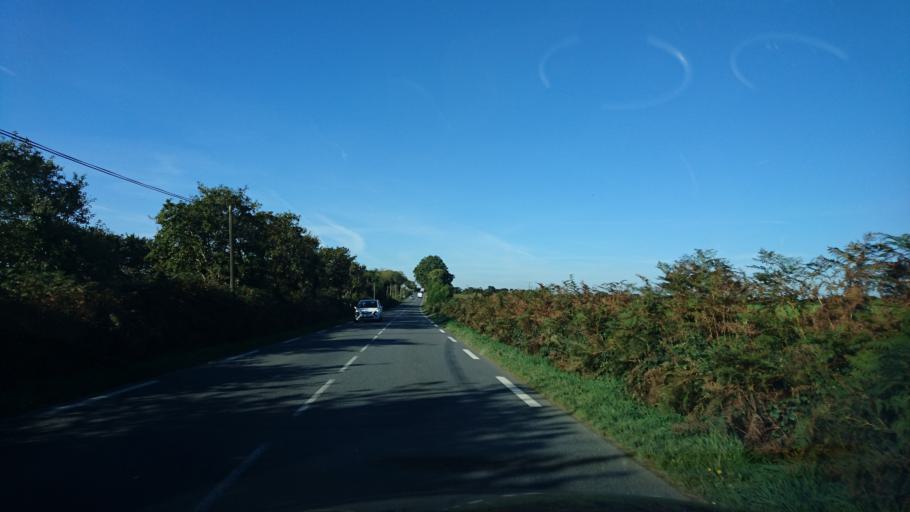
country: FR
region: Brittany
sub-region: Departement du Finistere
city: Guilers
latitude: 48.4495
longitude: -4.5382
